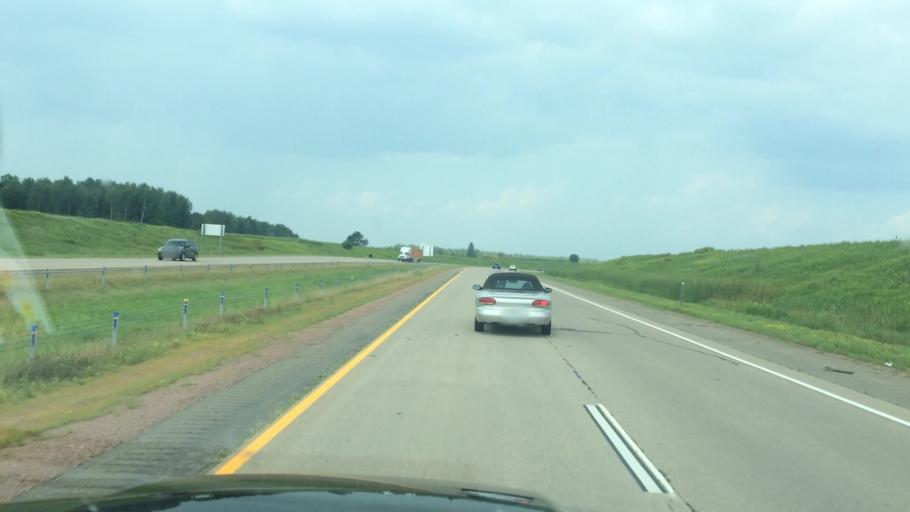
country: US
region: Wisconsin
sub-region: Clark County
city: Abbotsford
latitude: 44.9378
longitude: -90.2935
